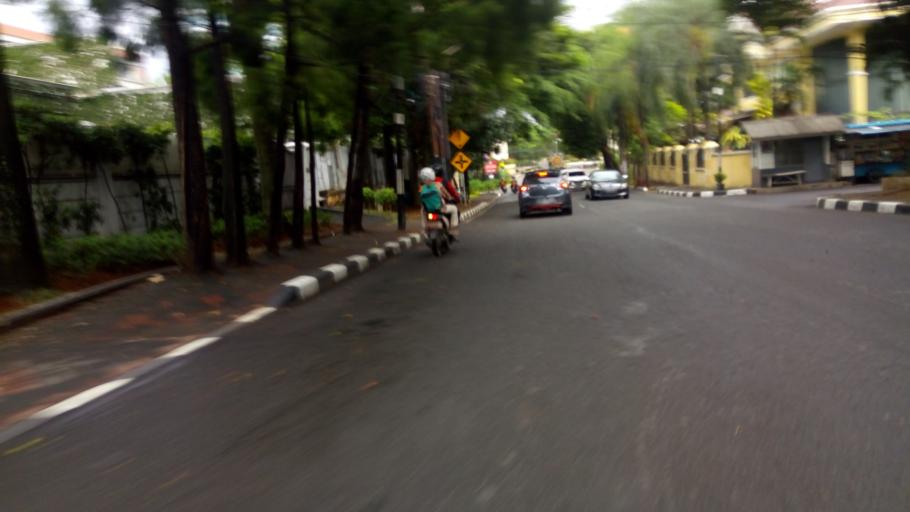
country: ID
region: Jakarta Raya
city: Jakarta
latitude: -6.2566
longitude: 106.8051
